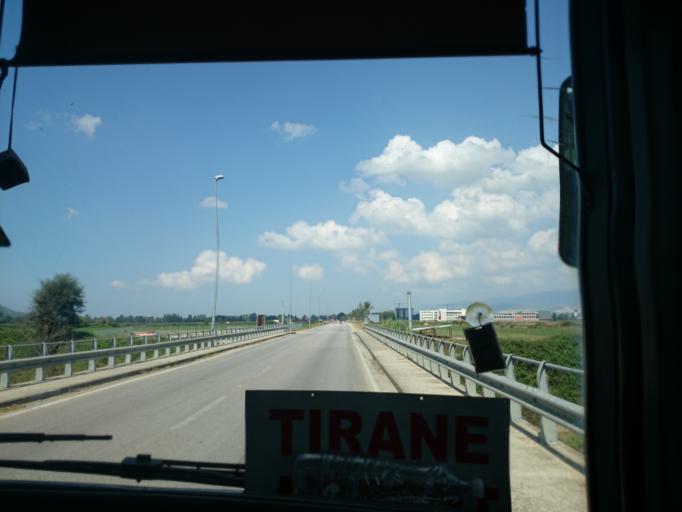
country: AL
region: Tirane
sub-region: Rrethi i Tiranes
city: Berxull
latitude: 41.3979
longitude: 19.7044
